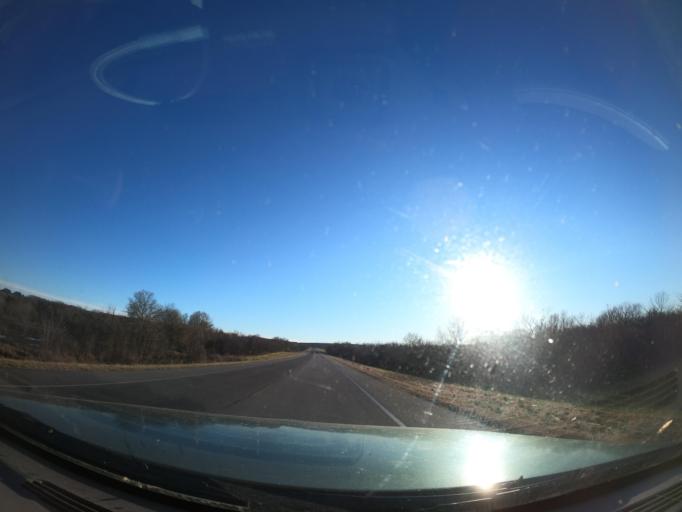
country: US
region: Oklahoma
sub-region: Pittsburg County
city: Hartshorne
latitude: 34.8535
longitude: -95.5347
